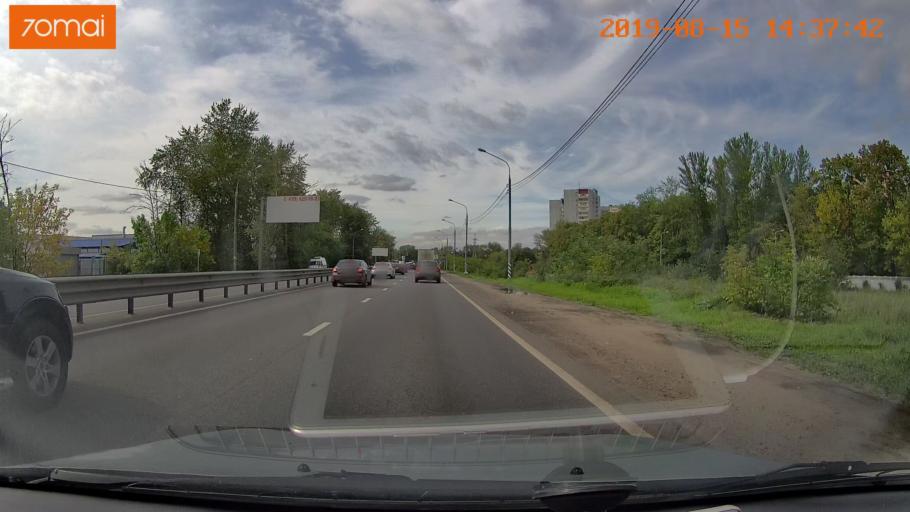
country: RU
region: Moskovskaya
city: Tomilino
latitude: 55.6543
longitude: 37.9241
